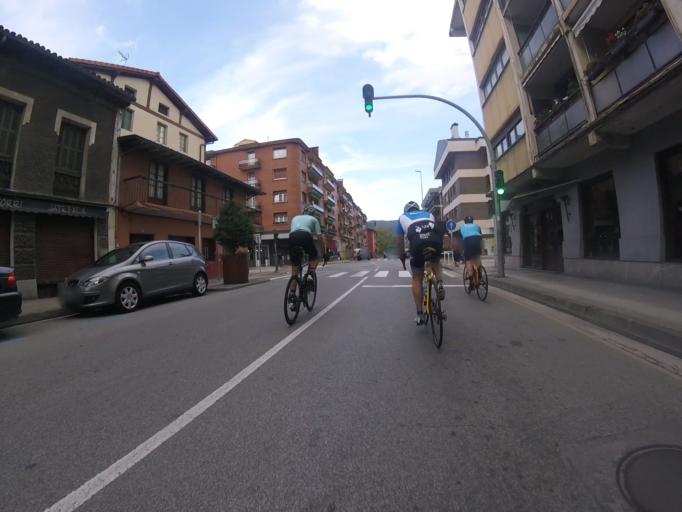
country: ES
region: Basque Country
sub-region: Provincia de Guipuzcoa
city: Villabona
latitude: 43.1891
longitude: -2.0527
